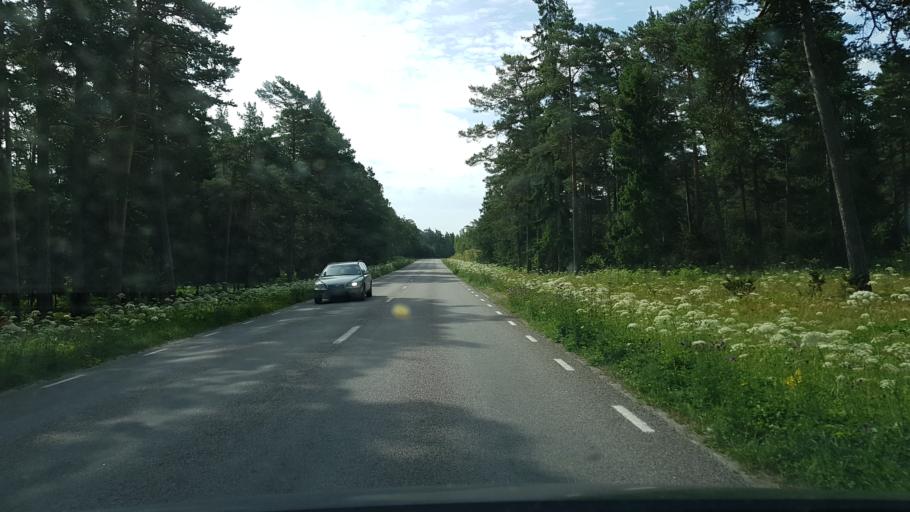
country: SE
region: Gotland
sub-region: Gotland
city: Hemse
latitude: 57.4590
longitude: 18.5748
